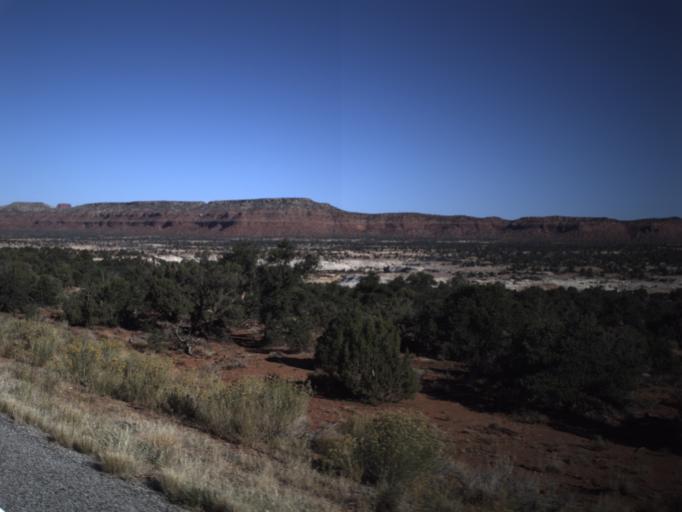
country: US
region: Utah
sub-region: San Juan County
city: Blanding
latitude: 37.6318
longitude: -110.0914
